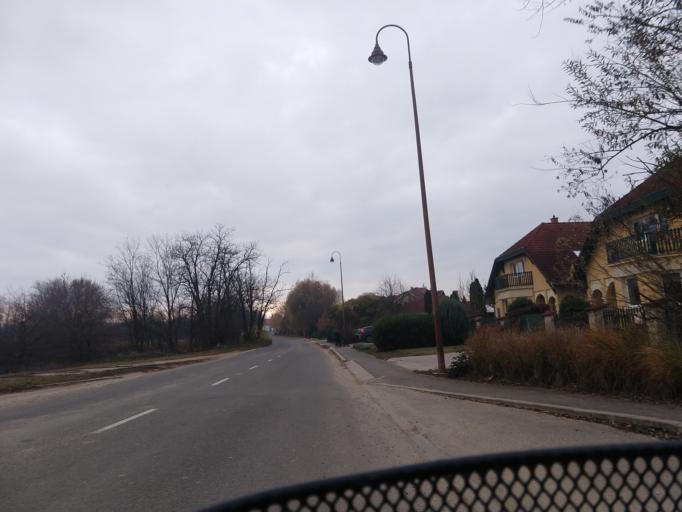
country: HU
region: Pest
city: Orbottyan
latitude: 47.6640
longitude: 19.2648
